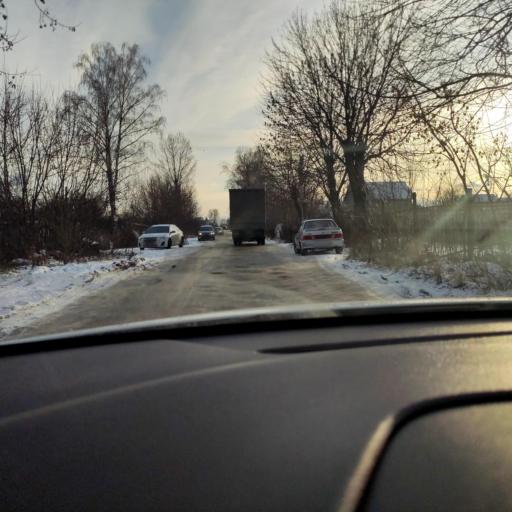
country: RU
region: Tatarstan
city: Staroye Arakchino
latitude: 55.8657
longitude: 49.0469
